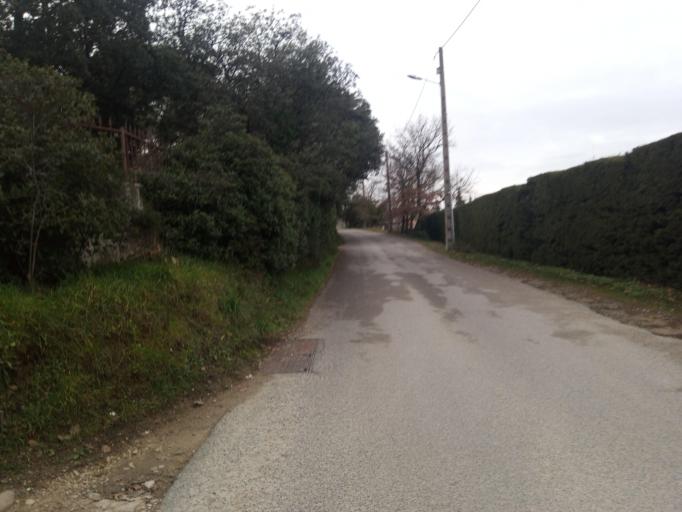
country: FR
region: Provence-Alpes-Cote d'Azur
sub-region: Departement du Vaucluse
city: Lauris
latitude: 43.7475
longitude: 5.3230
